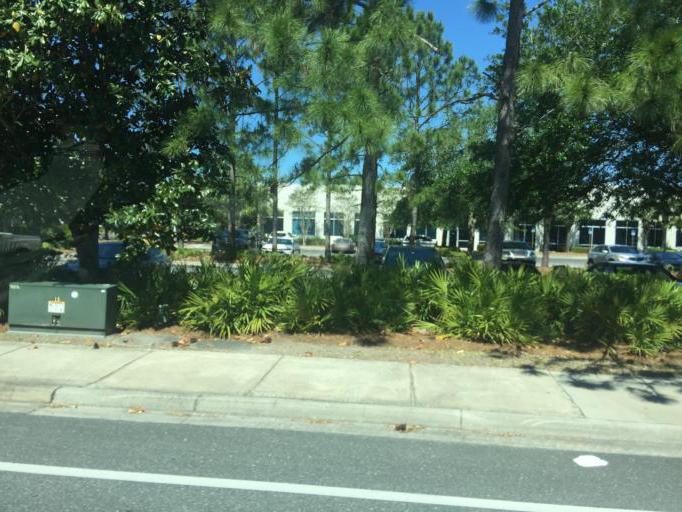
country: US
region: Florida
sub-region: Bay County
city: Panama City Beach
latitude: 30.1919
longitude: -85.8145
